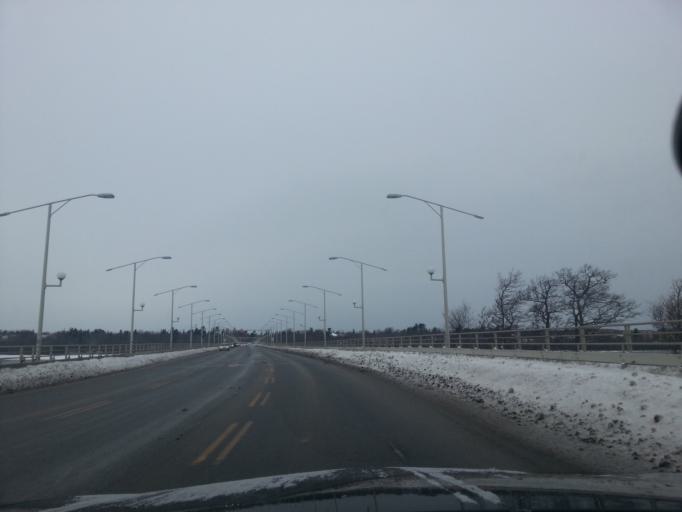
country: CA
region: Ontario
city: Ottawa
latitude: 45.4085
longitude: -75.7572
